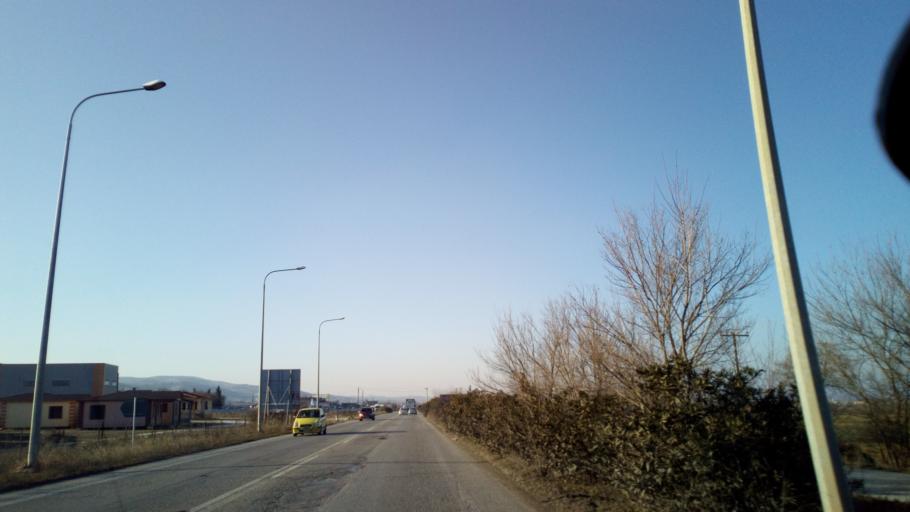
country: GR
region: Central Macedonia
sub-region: Nomos Thessalonikis
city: Kavallari
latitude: 40.7136
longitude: 23.0298
